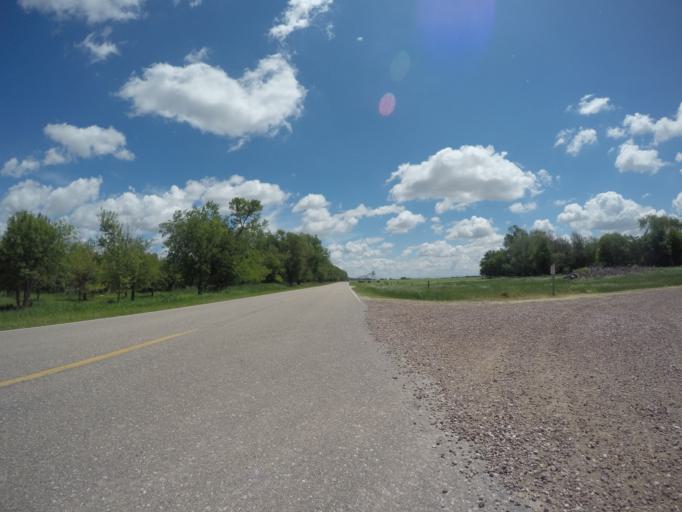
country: US
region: Nebraska
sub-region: Buffalo County
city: Kearney
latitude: 40.6547
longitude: -99.1214
